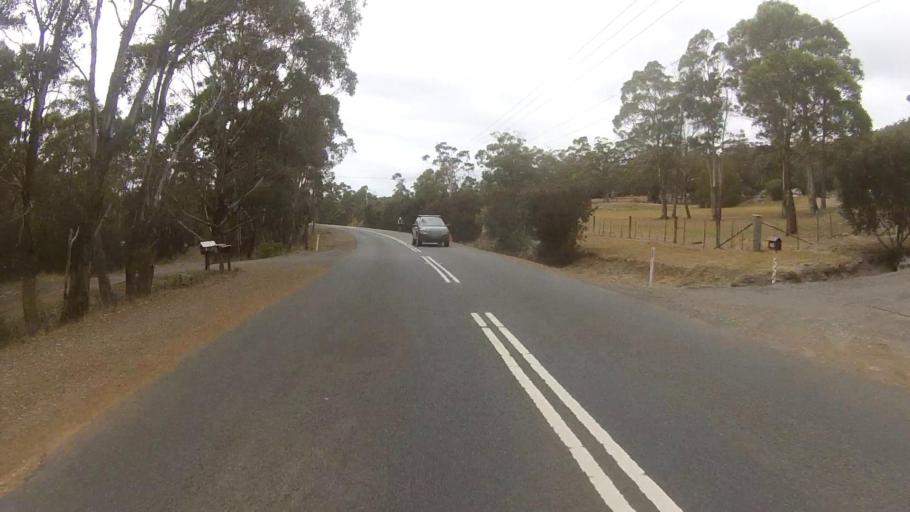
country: AU
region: Tasmania
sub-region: Kingborough
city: Margate
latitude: -43.0013
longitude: 147.2322
